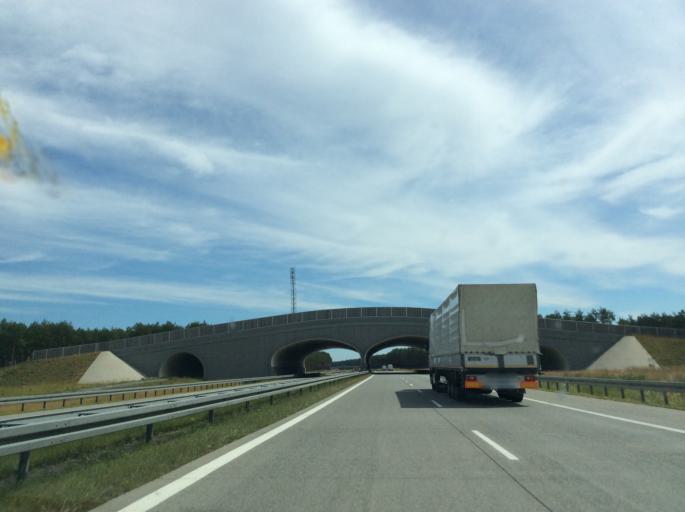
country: PL
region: Greater Poland Voivodeship
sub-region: Powiat nowotomyski
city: Miedzichowo
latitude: 52.3298
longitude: 15.9261
